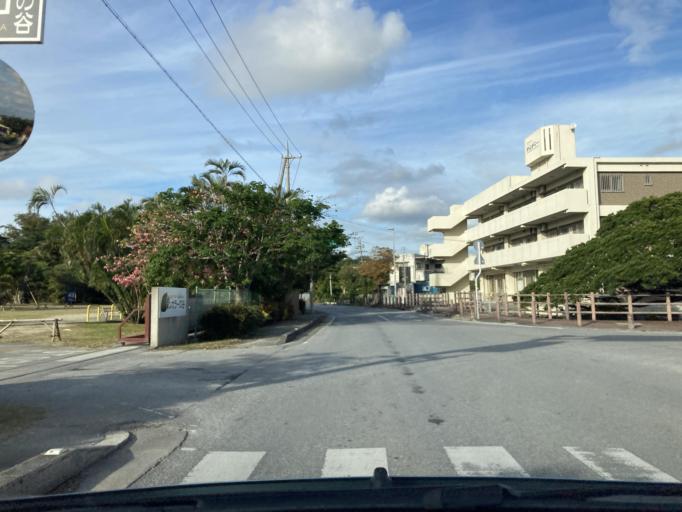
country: JP
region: Okinawa
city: Tomigusuku
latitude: 26.1407
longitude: 127.7475
